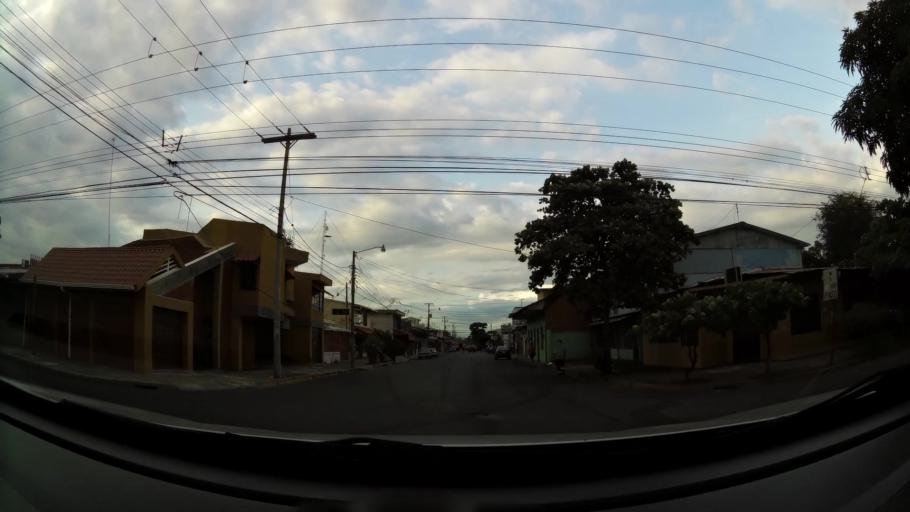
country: CR
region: Puntarenas
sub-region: Canton Central de Puntarenas
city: Puntarenas
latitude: 9.9768
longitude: -84.8294
